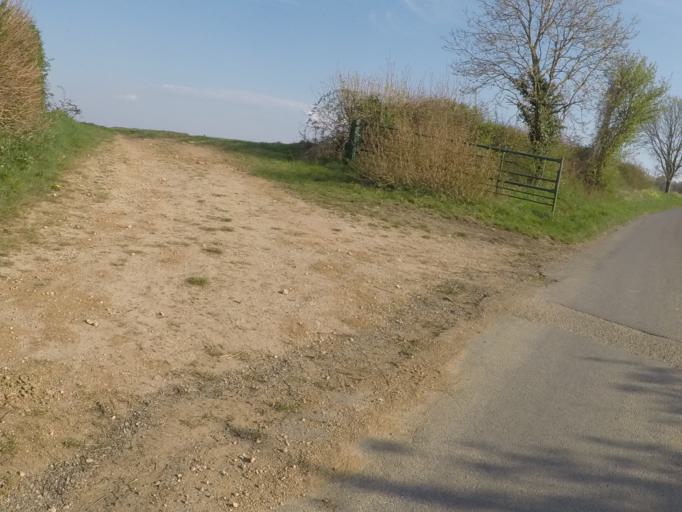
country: GB
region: England
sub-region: Oxfordshire
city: Charlbury
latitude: 51.8776
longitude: -1.5167
